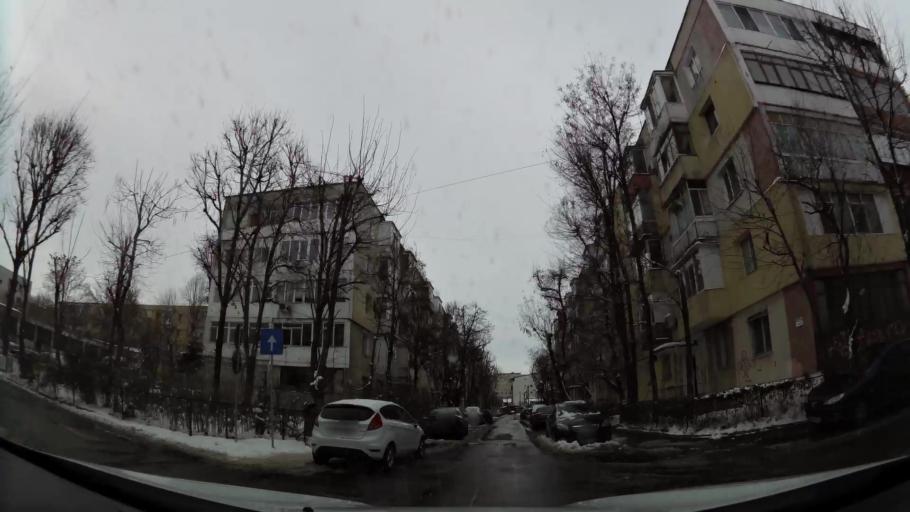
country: RO
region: Ilfov
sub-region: Comuna Popesti-Leordeni
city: Popesti-Leordeni
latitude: 44.3868
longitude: 26.1325
